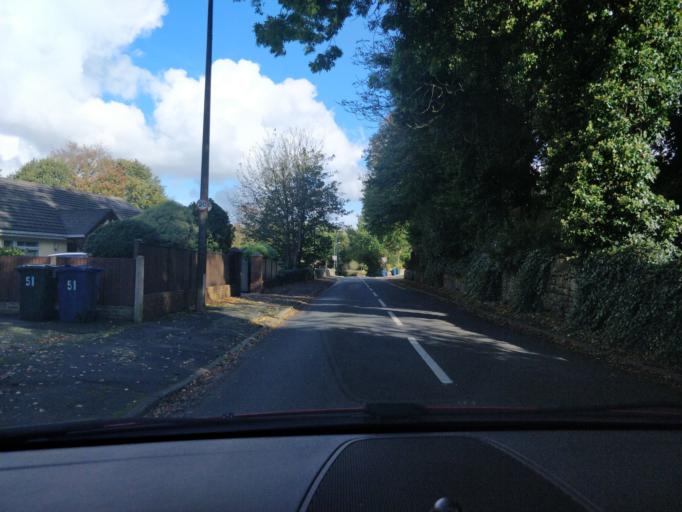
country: GB
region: England
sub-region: Lancashire
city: Ormskirk
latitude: 53.5709
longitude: -2.8716
